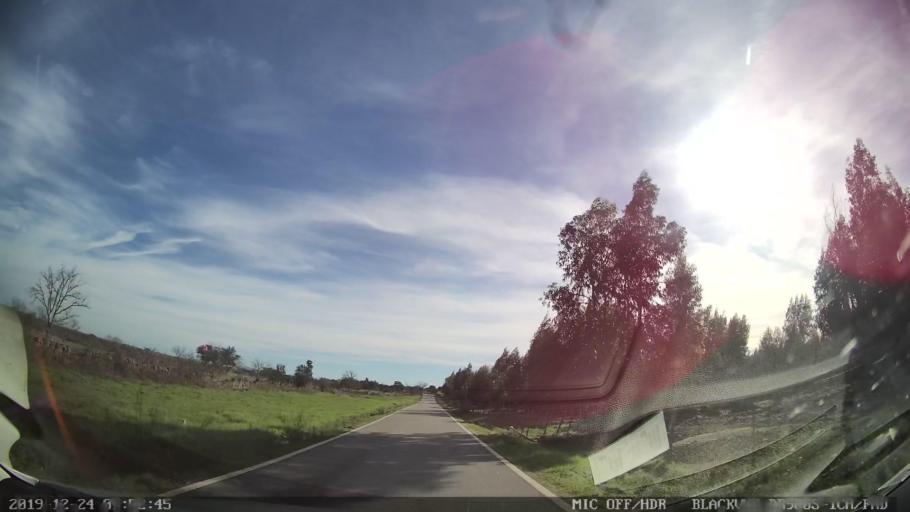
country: PT
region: Portalegre
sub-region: Nisa
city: Nisa
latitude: 39.4904
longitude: -7.7422
